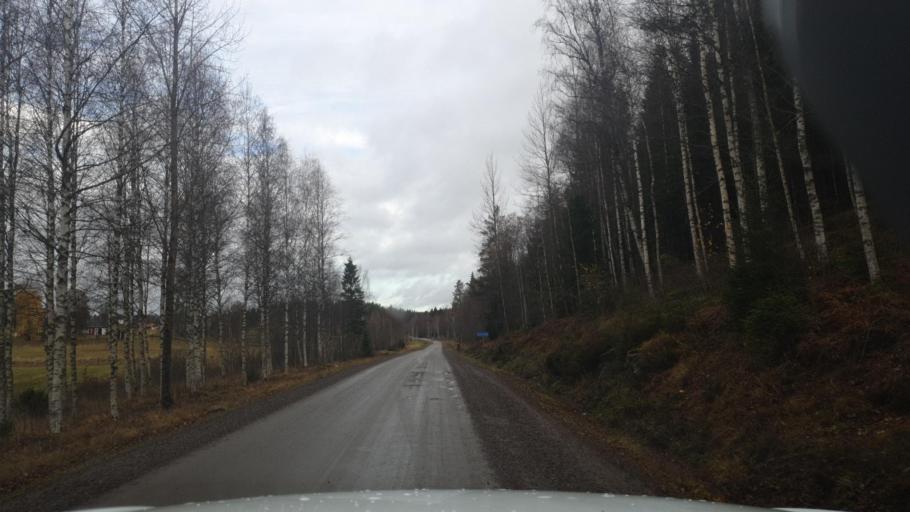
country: NO
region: Ostfold
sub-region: Romskog
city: Romskog
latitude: 59.8455
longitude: 11.9831
